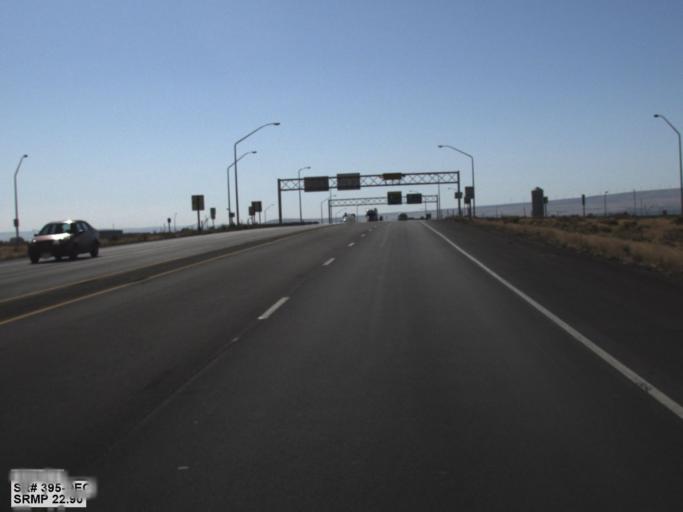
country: US
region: Washington
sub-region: Franklin County
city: Pasco
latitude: 46.2540
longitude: -119.0833
